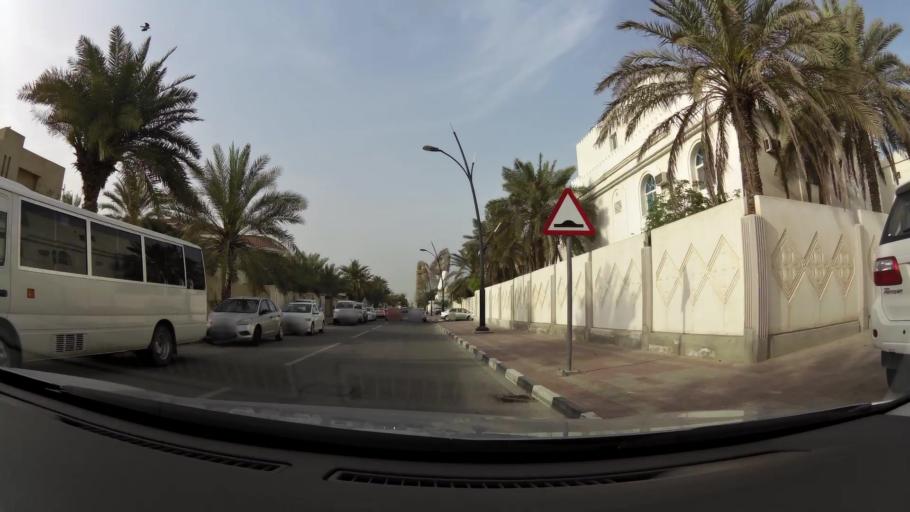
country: QA
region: Baladiyat ad Dawhah
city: Doha
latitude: 25.3288
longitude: 51.5176
